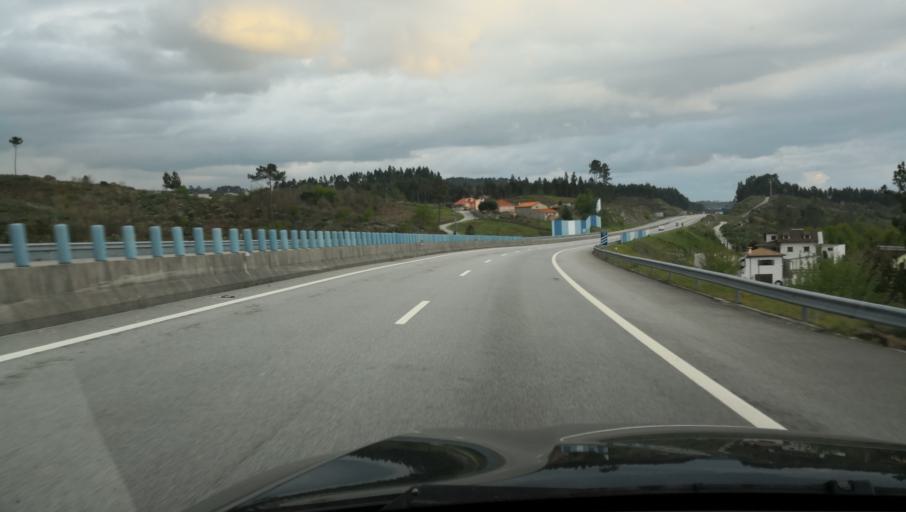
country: PT
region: Viseu
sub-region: Viseu
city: Viseu
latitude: 40.6367
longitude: -7.9578
